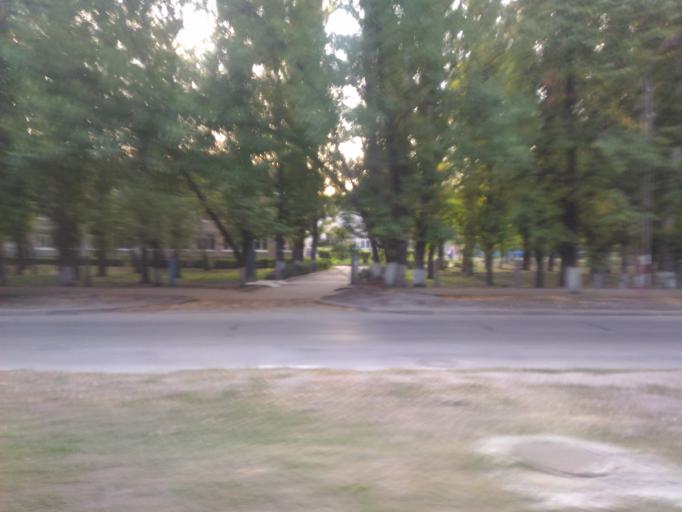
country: RU
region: Ulyanovsk
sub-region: Ulyanovskiy Rayon
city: Ulyanovsk
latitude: 54.2999
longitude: 48.3215
